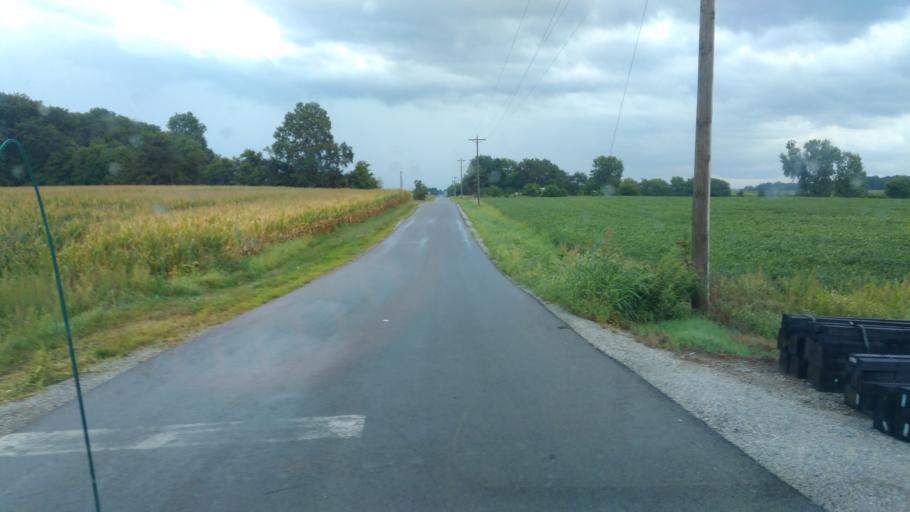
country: US
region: Ohio
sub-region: Hardin County
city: Kenton
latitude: 40.6895
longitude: -83.6433
